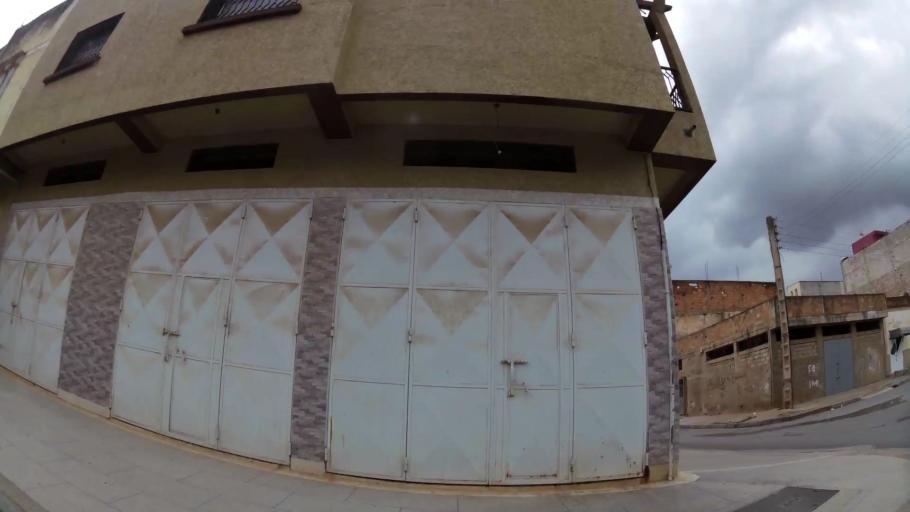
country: MA
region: Rabat-Sale-Zemmour-Zaer
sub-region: Khemisset
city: Tiflet
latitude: 33.8932
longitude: -6.3286
